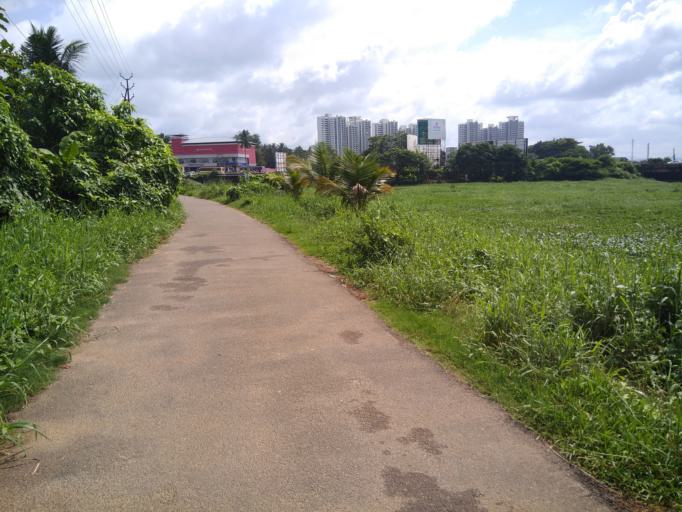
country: IN
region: Kerala
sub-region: Thrissur District
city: Trichur
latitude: 10.5443
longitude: 76.1785
